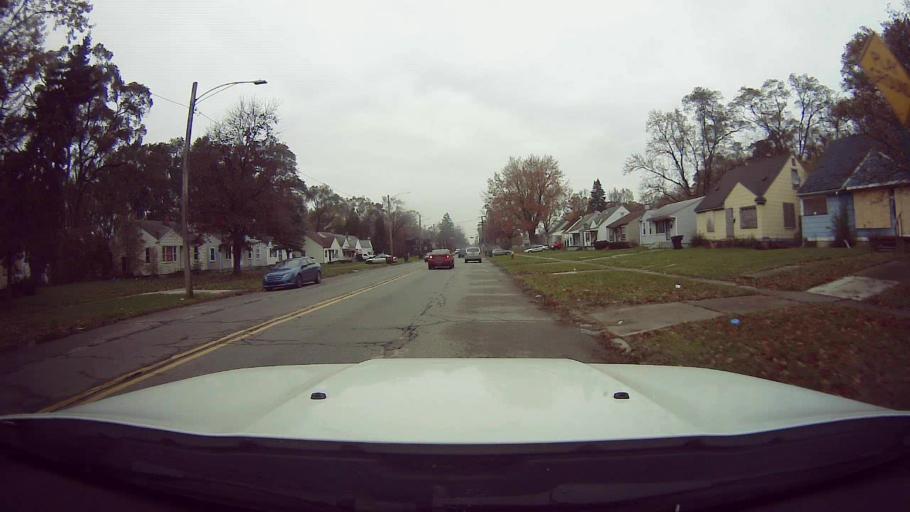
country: US
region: Michigan
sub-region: Wayne County
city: Redford
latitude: 42.4062
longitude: -83.2570
